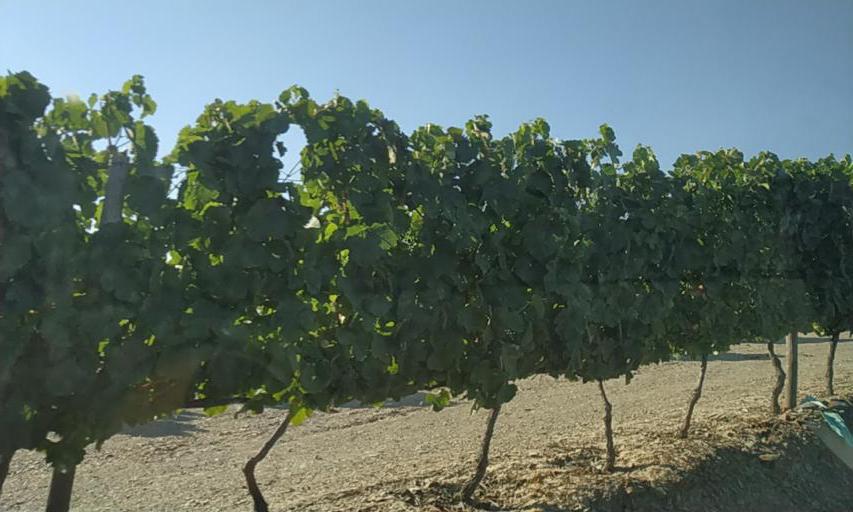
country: PT
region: Viseu
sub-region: Sao Joao da Pesqueira
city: Sao Joao da Pesqueira
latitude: 41.1580
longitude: -7.4179
